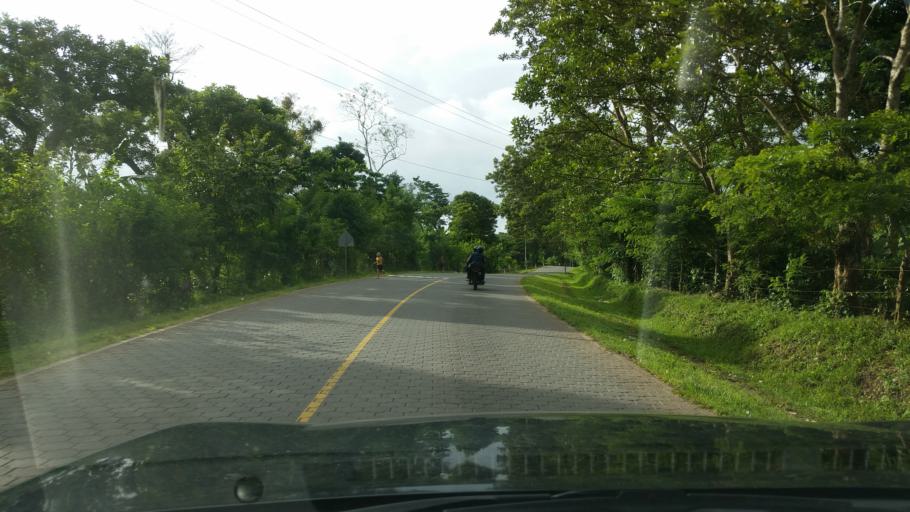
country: NI
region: Matagalpa
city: San Ramon
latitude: 13.1670
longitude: -85.7274
